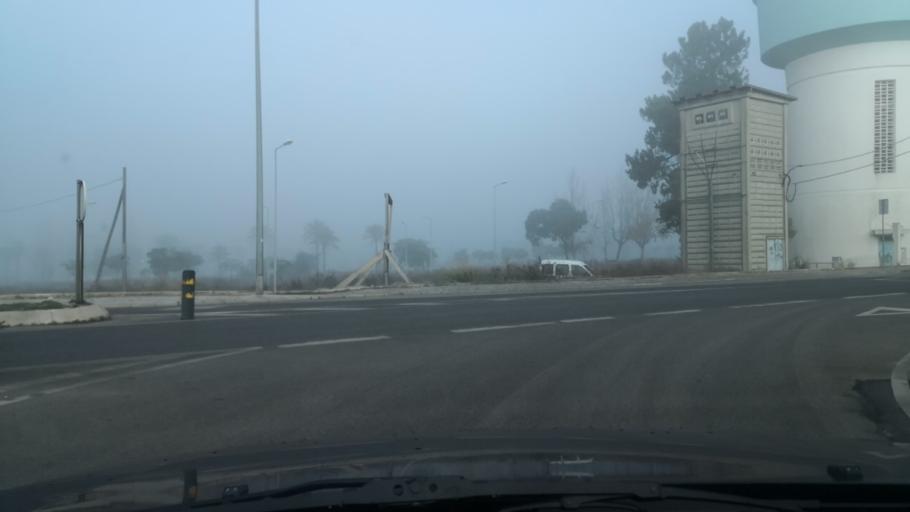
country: PT
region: Setubal
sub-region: Palmela
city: Pinhal Novo
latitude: 38.6191
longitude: -8.9168
